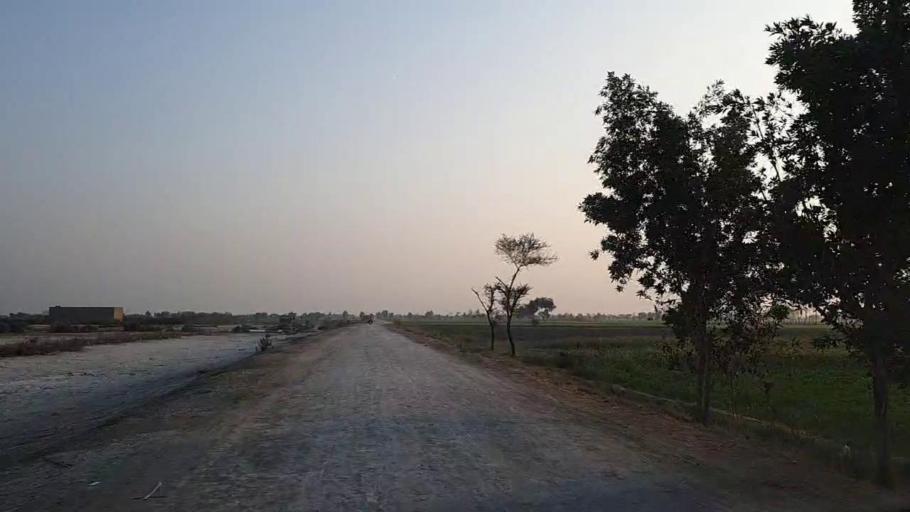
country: PK
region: Sindh
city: Daur
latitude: 26.4259
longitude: 68.3680
